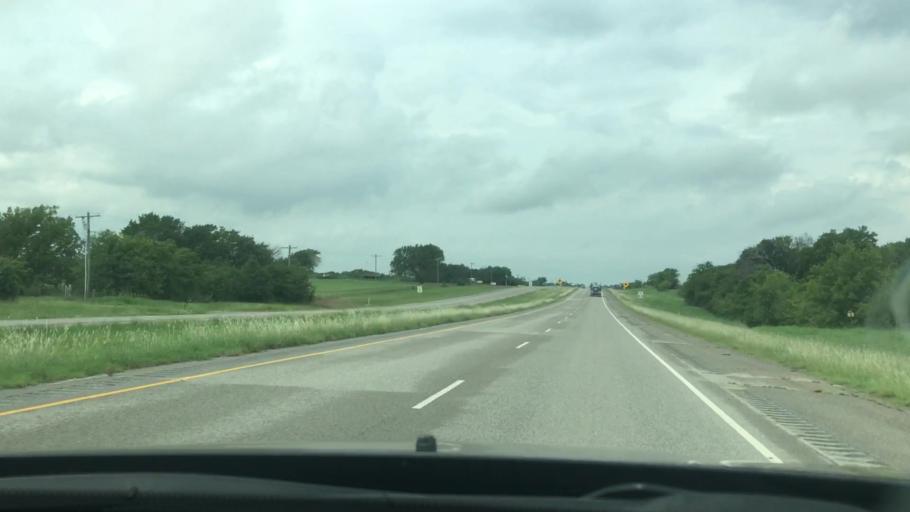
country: US
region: Oklahoma
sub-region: Carter County
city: Wilson
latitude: 34.1731
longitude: -97.4670
